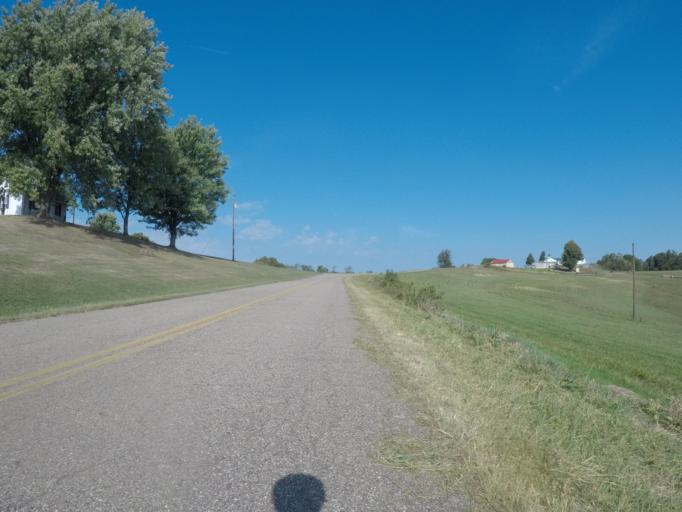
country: US
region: West Virginia
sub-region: Cabell County
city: Lesage
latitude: 38.6479
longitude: -82.4195
